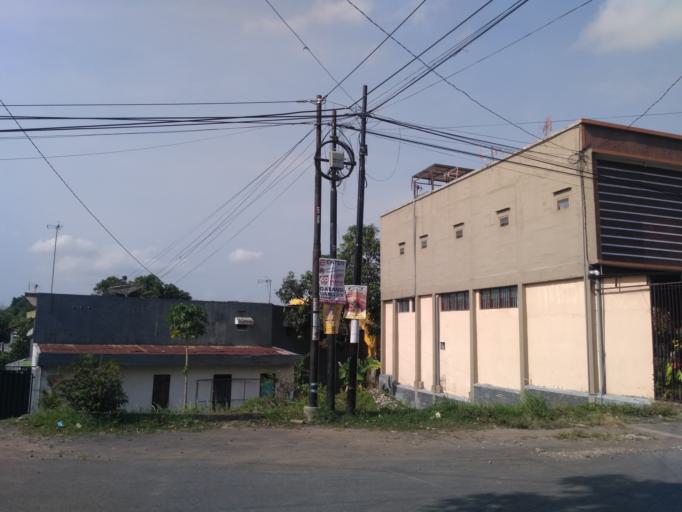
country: ID
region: East Java
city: Malang
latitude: -7.9383
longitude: 112.6096
